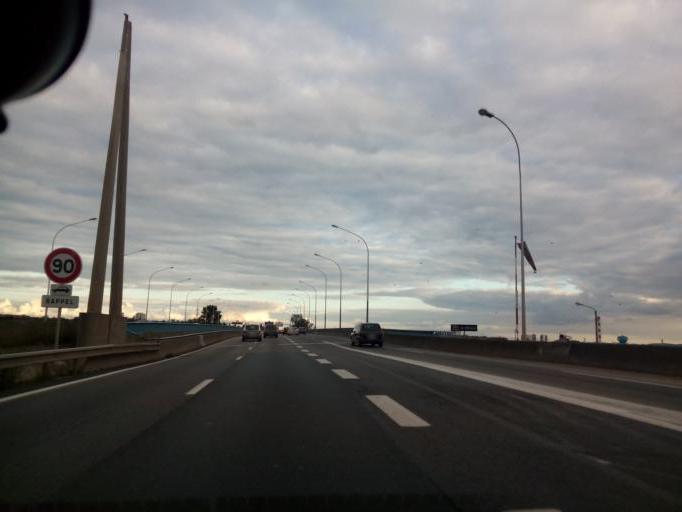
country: FR
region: Rhone-Alpes
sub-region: Departement du Rhone
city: Pierre-Benite
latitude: 45.6968
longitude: 4.8378
